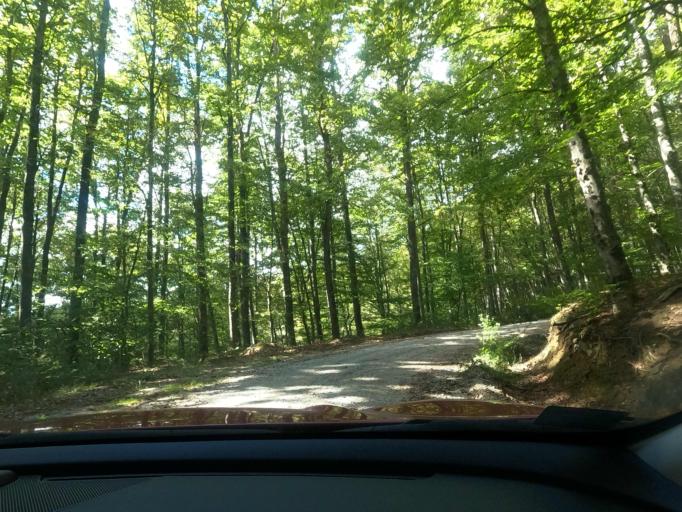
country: BA
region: Federation of Bosnia and Herzegovina
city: Velika Kladusa
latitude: 45.2478
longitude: 15.7708
